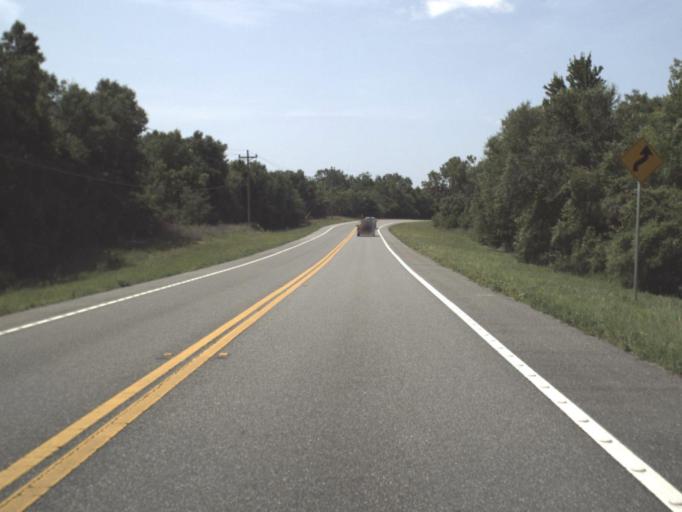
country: US
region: Florida
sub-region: Taylor County
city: Steinhatchee
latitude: 29.7125
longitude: -83.3587
